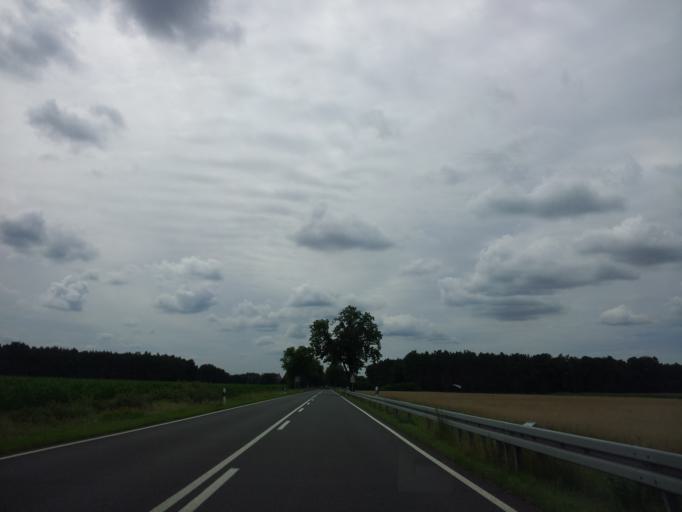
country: DE
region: Brandenburg
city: Treuenbrietzen
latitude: 52.1351
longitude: 12.9098
